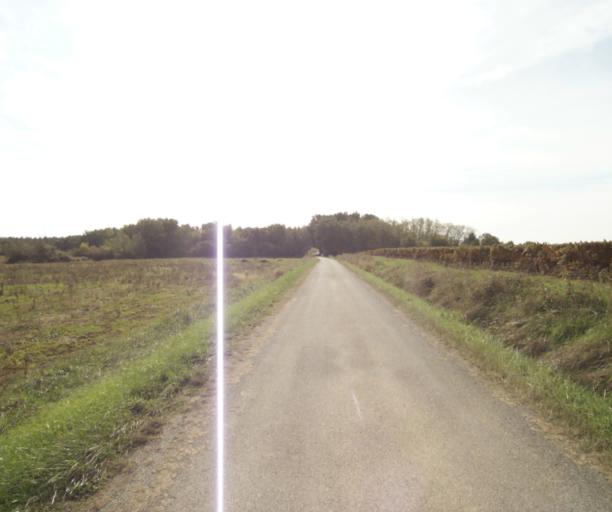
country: FR
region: Midi-Pyrenees
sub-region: Departement du Tarn-et-Garonne
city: Orgueil
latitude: 43.8875
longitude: 1.4028
